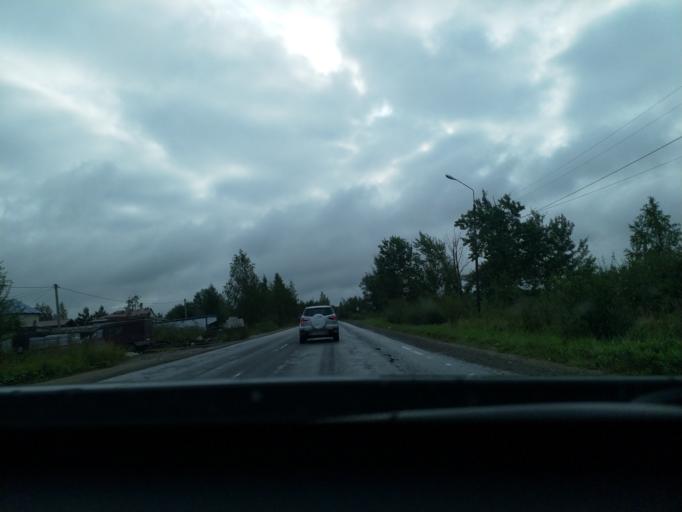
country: RU
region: Leningrad
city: Nikol'skoye
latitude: 59.6921
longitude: 30.7971
